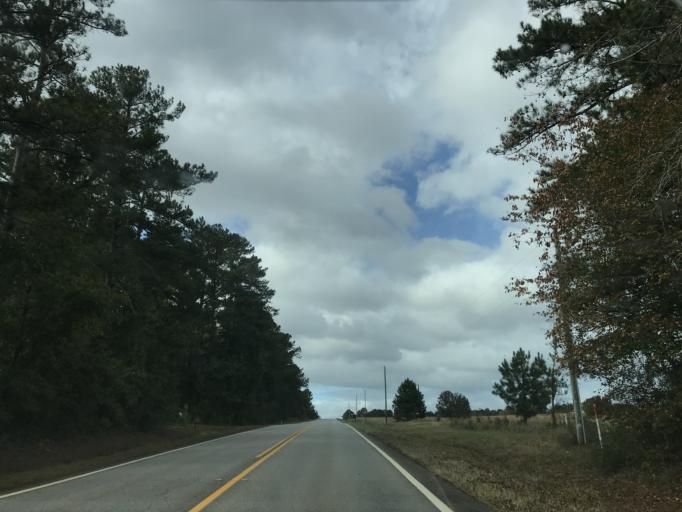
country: US
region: Georgia
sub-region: Jones County
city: Gray
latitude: 32.9773
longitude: -83.5047
